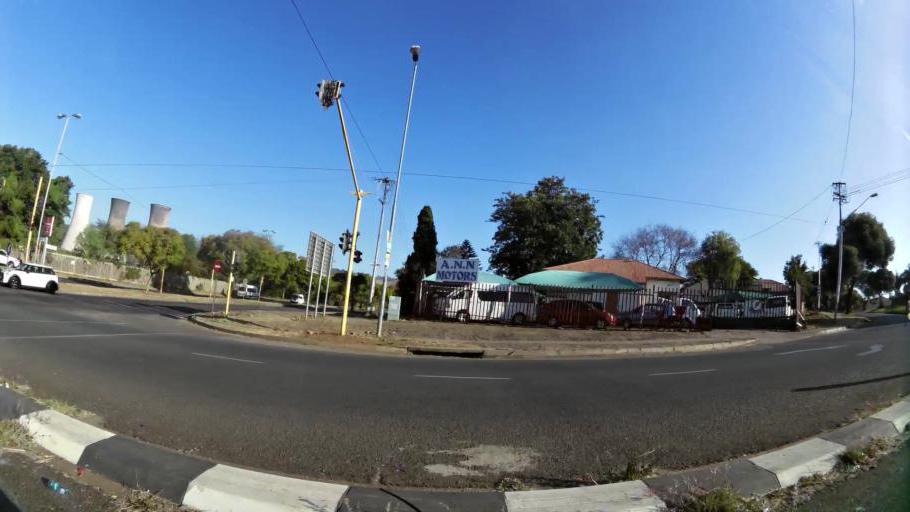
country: ZA
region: Gauteng
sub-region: City of Tshwane Metropolitan Municipality
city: Pretoria
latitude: -25.7542
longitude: 28.1430
